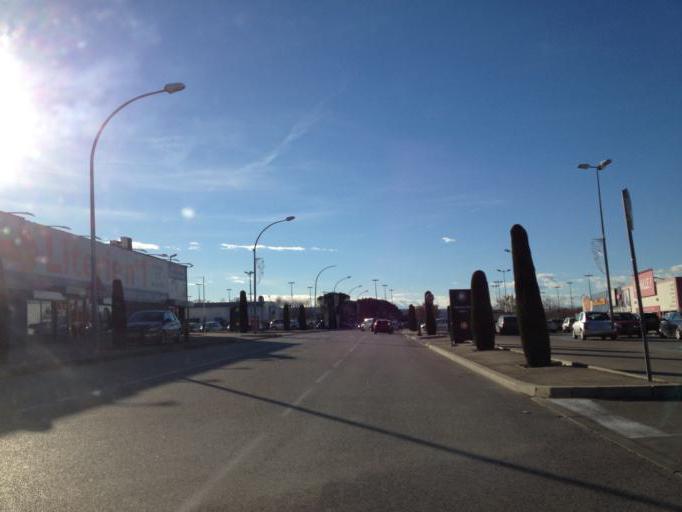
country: FR
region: Provence-Alpes-Cote d'Azur
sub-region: Departement du Vaucluse
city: Vedene
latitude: 43.9849
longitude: 4.8858
